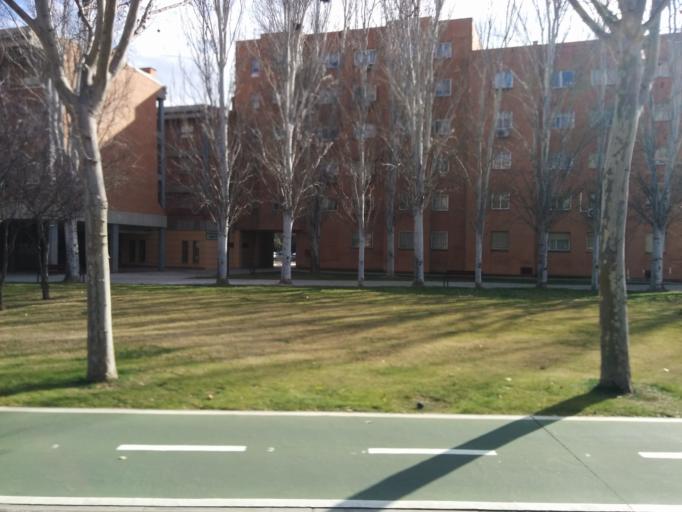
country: ES
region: Aragon
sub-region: Provincia de Zaragoza
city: Zaragoza
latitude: 41.6645
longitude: -0.8868
